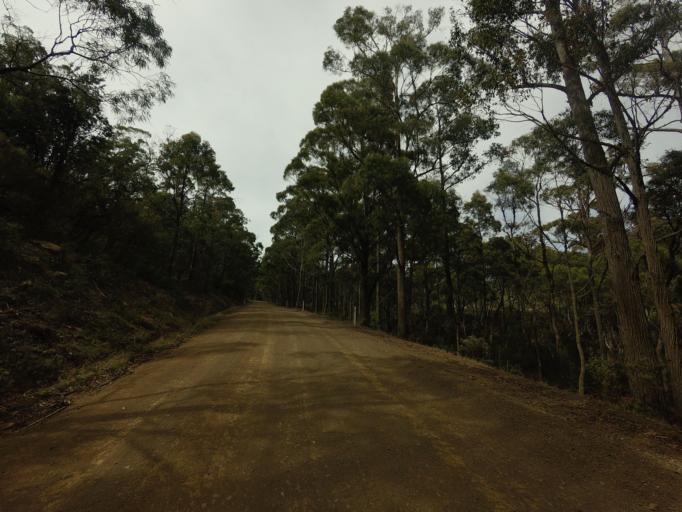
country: AU
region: Tasmania
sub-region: Sorell
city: Sorell
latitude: -42.4818
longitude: 147.6146
